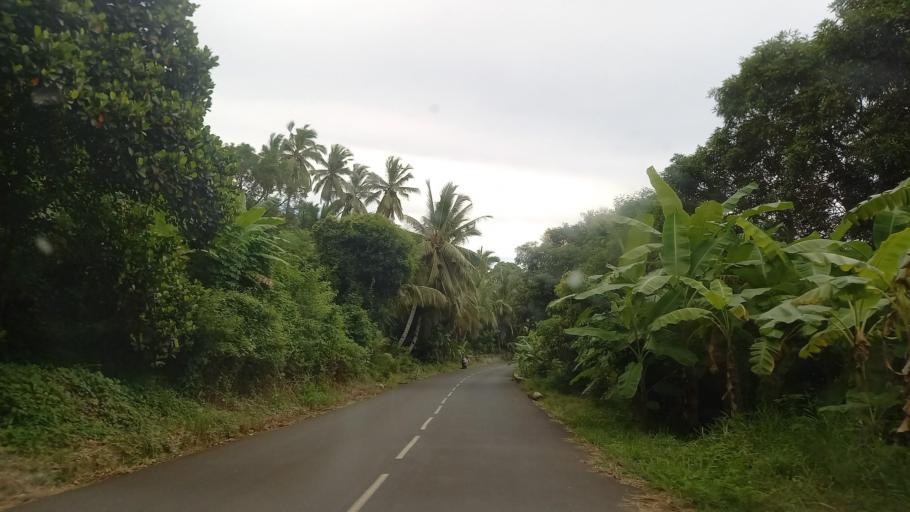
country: YT
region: Boueni
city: Boueni
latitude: -12.9031
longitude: 45.0861
